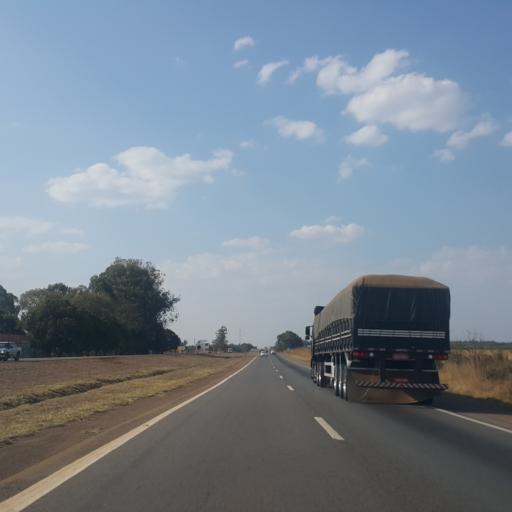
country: BR
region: Goias
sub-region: Abadiania
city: Abadiania
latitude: -16.2390
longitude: -48.7603
